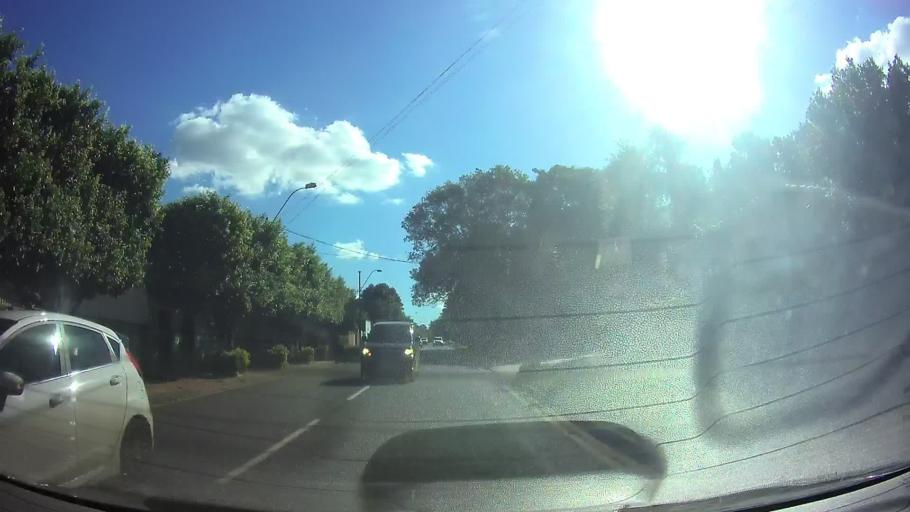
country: PY
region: Cordillera
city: Caacupe
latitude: -25.3928
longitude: -57.1423
